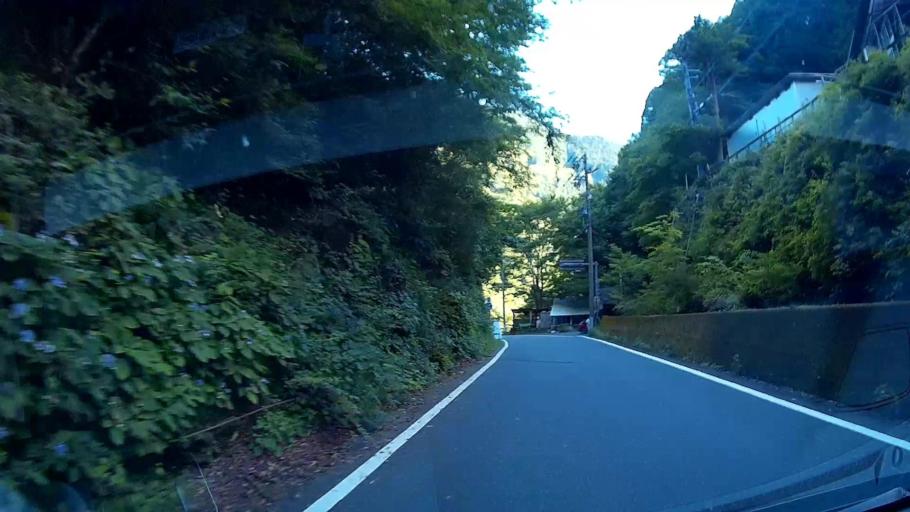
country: JP
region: Shizuoka
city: Shizuoka-shi
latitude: 35.2124
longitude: 138.2215
